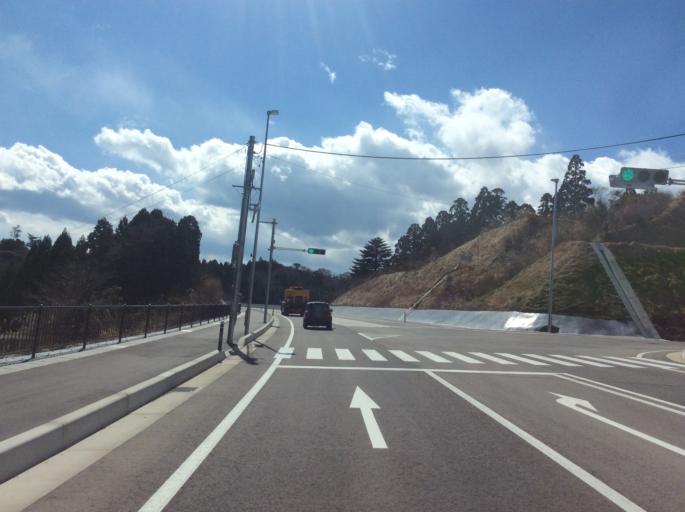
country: JP
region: Fukushima
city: Iwaki
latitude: 37.1219
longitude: 140.9930
